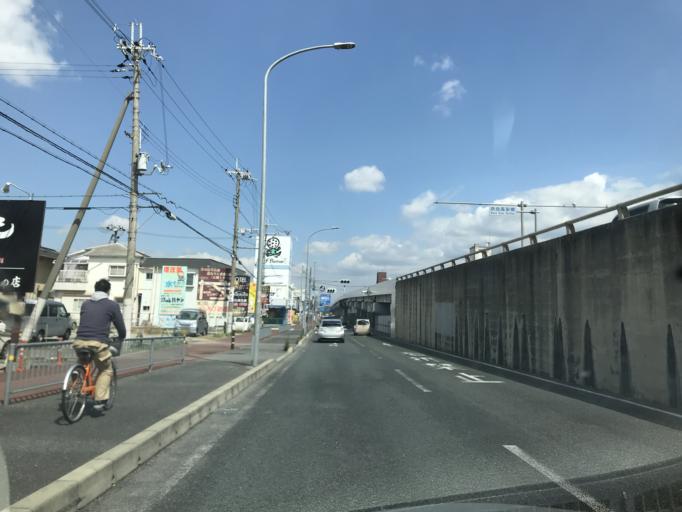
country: JP
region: Nara
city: Nara-shi
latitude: 34.6800
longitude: 135.8002
